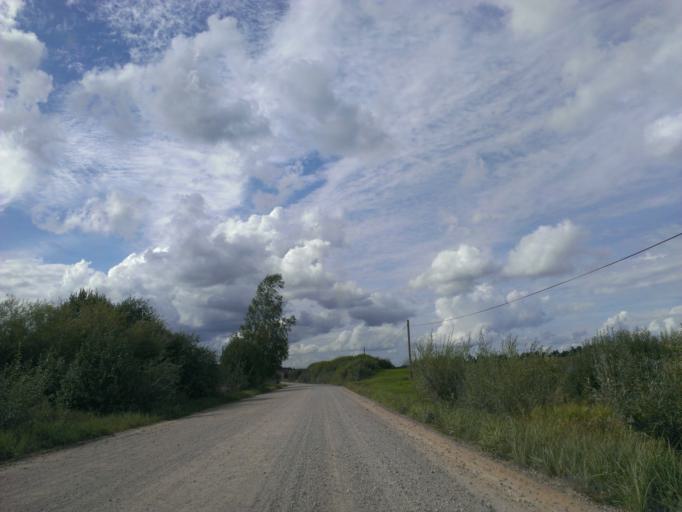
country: LV
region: Skriveri
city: Skriveri
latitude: 56.8445
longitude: 25.1732
